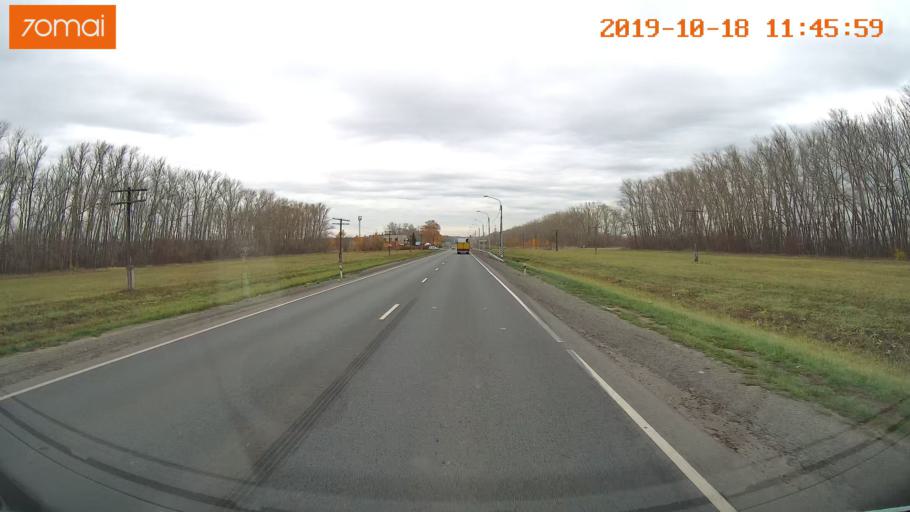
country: RU
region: Rjazan
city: Mikhaylov
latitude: 54.2156
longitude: 38.9776
